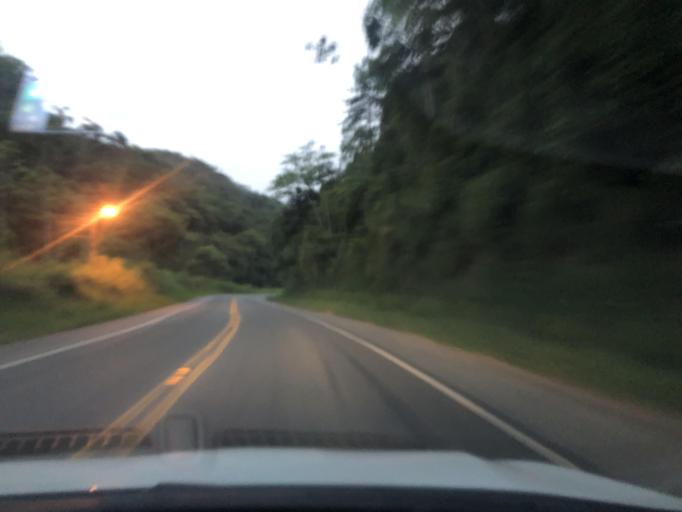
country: BR
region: Santa Catarina
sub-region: Pomerode
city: Pomerode
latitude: -26.6610
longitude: -49.0311
